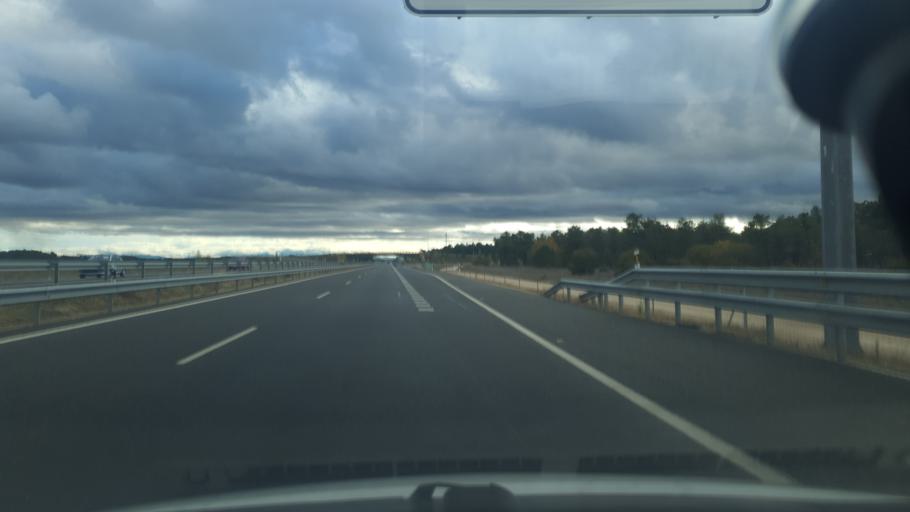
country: ES
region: Castille and Leon
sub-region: Provincia de Segovia
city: Sanchonuno
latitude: 41.2997
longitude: -4.3014
